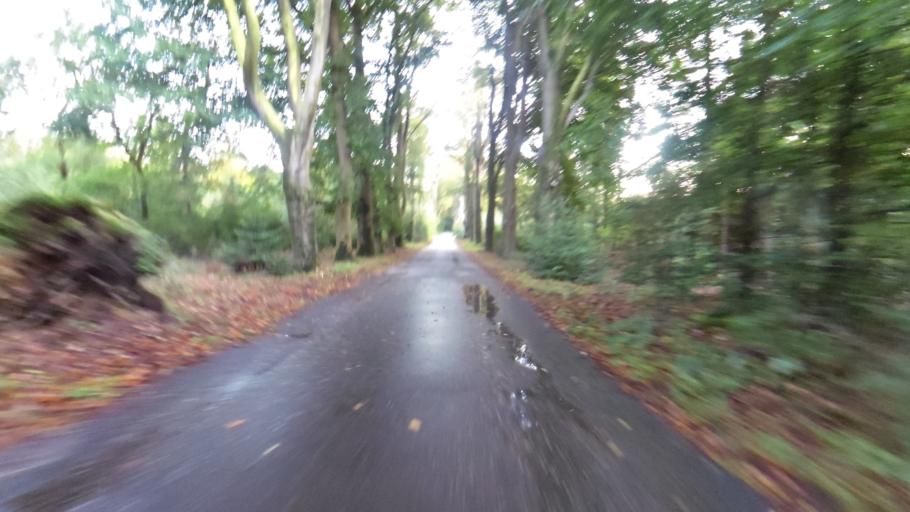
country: NL
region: Utrecht
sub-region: Gemeente Utrechtse Heuvelrug
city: Amerongen
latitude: 52.0239
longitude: 5.4606
